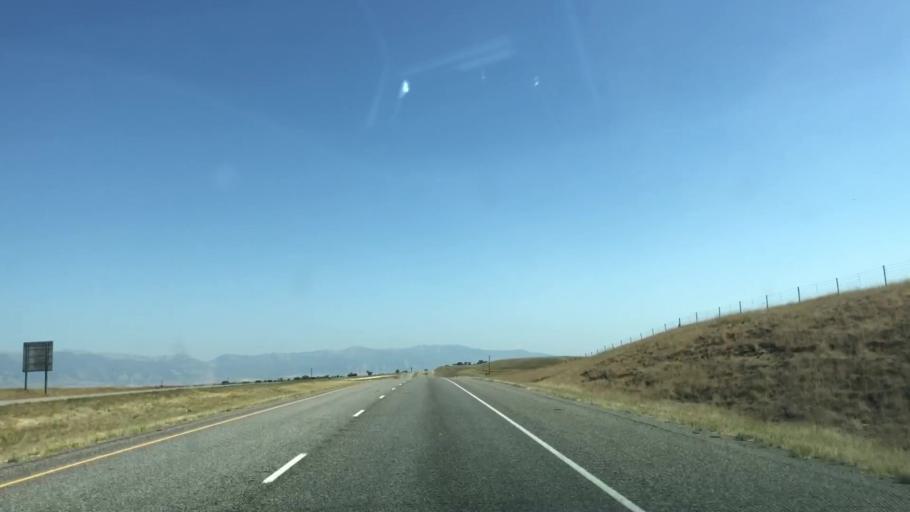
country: US
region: Montana
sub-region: Gallatin County
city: Manhattan
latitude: 45.8797
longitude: -111.4125
